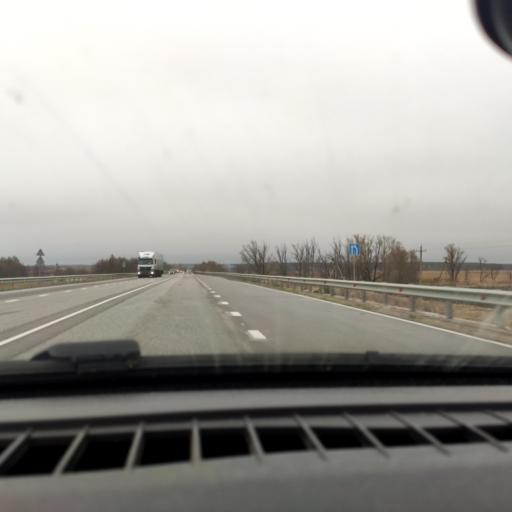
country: RU
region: Voronezj
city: Ostrogozhsk
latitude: 51.0298
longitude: 38.9867
